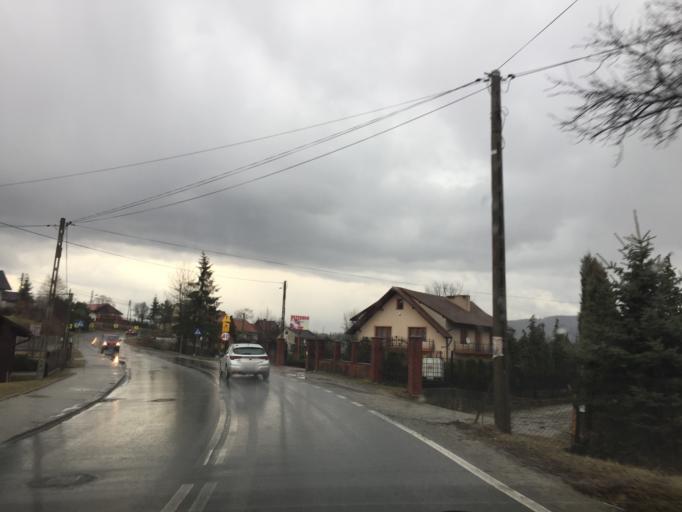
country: PL
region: Lesser Poland Voivodeship
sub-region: Powiat myslenicki
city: Harbutowice
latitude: 49.8241
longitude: 19.7901
